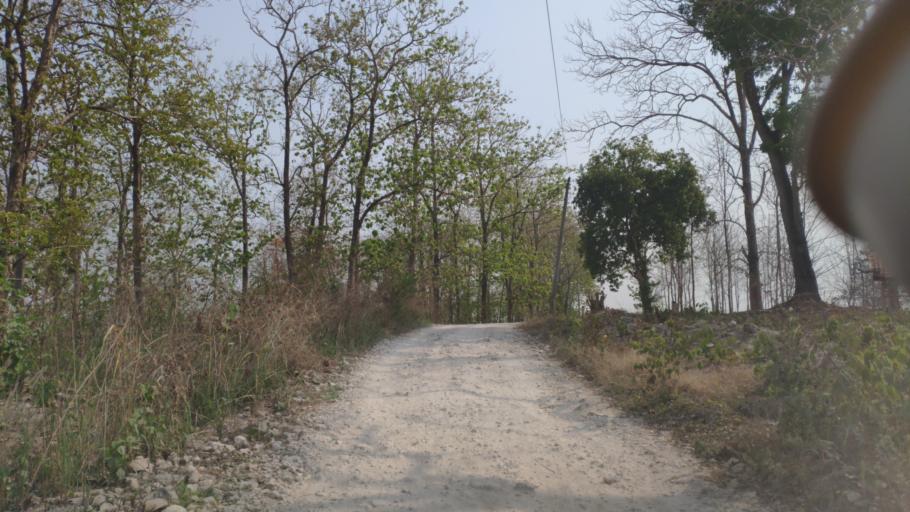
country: ID
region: Central Java
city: Randublatung
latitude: -7.2575
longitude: 111.2736
